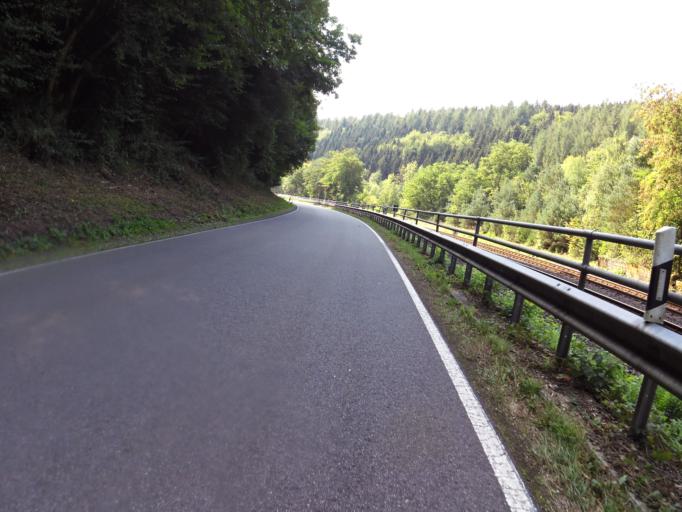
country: DE
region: Rheinland-Pfalz
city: Speicher
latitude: 49.9314
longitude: 6.6150
